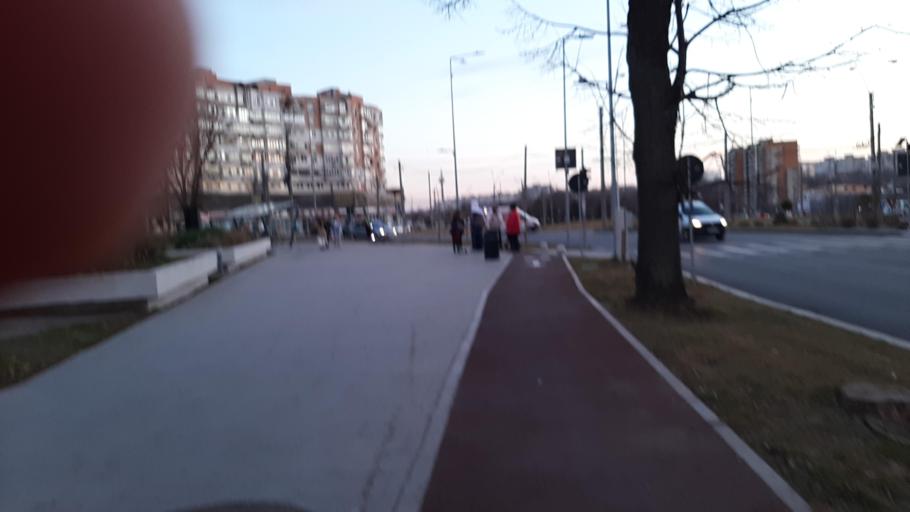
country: RO
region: Galati
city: Galati
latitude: 45.4283
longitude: 28.0248
